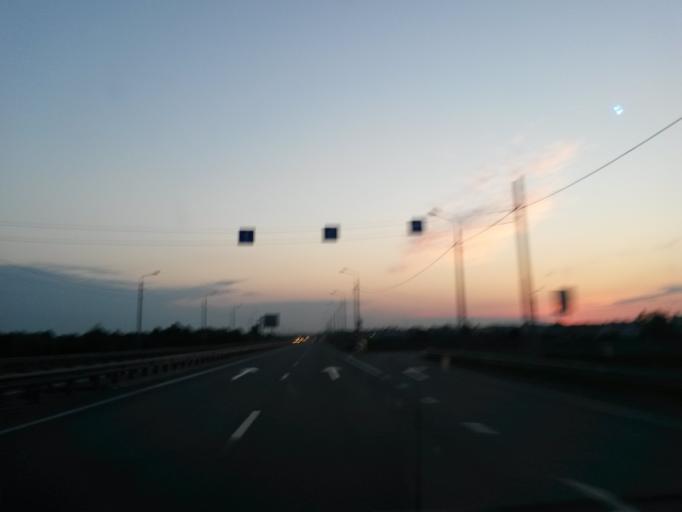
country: RU
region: Jaroslavl
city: Yaroslavl
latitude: 57.6677
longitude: 39.8166
